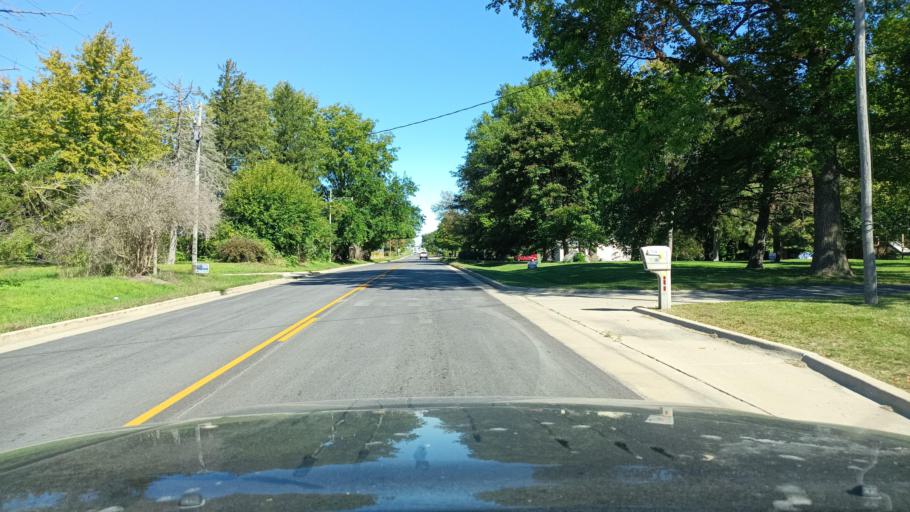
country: US
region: Illinois
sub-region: Champaign County
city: Philo
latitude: 40.0008
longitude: -88.1614
